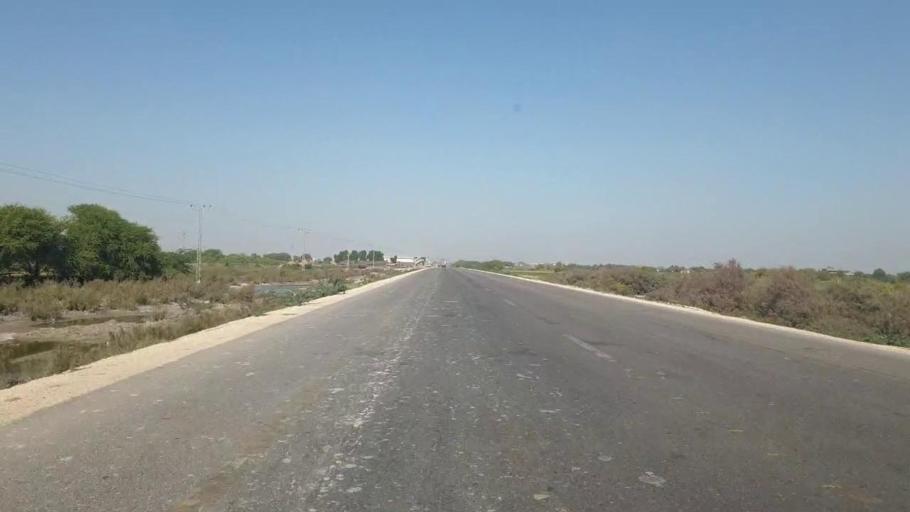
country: PK
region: Sindh
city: Talhar
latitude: 24.8573
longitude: 68.8165
